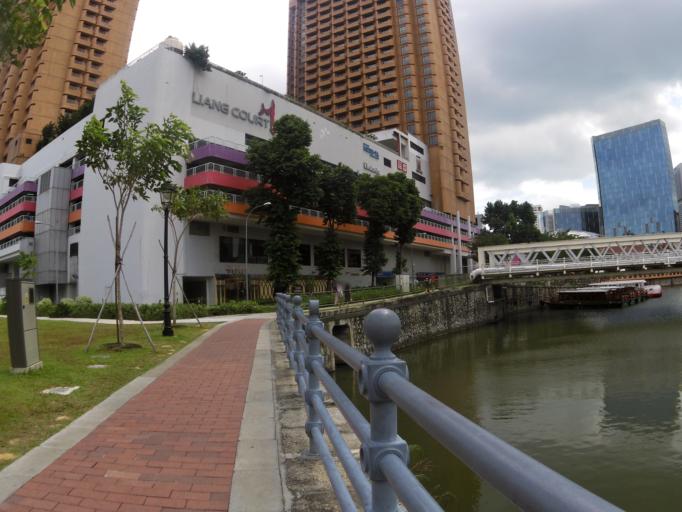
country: SG
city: Singapore
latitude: 1.2913
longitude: 103.8437
